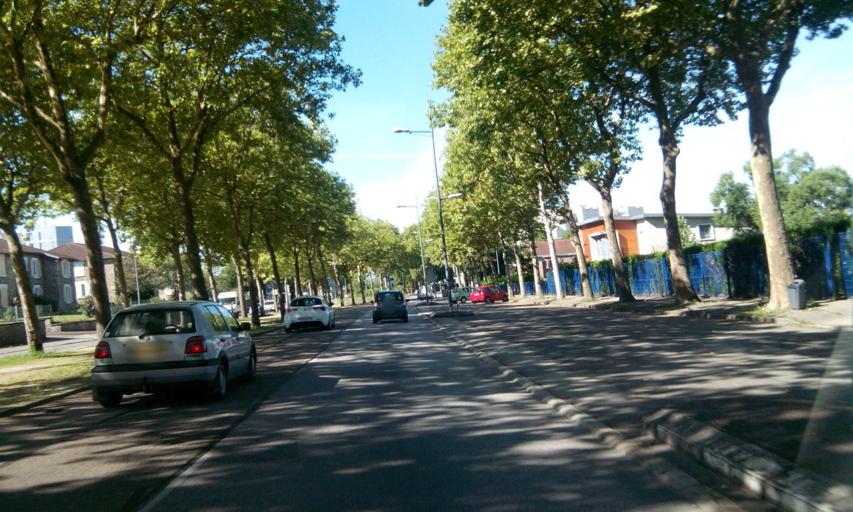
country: FR
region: Limousin
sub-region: Departement de la Haute-Vienne
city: Limoges
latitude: 45.8457
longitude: 1.2422
